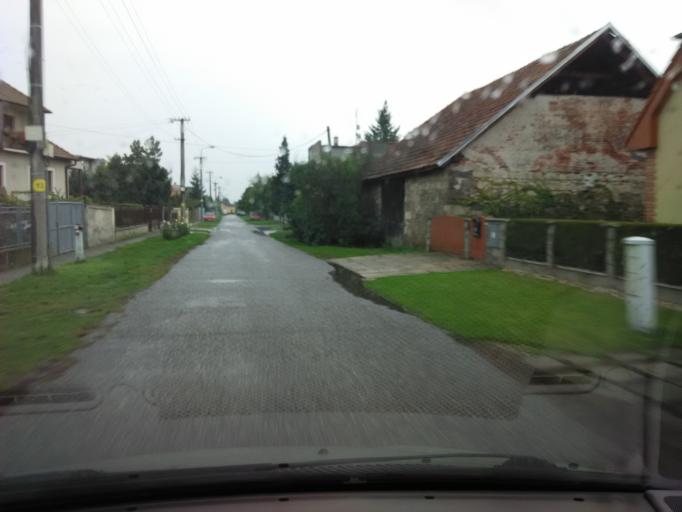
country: SK
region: Nitriansky
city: Levice
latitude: 48.2438
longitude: 18.5665
